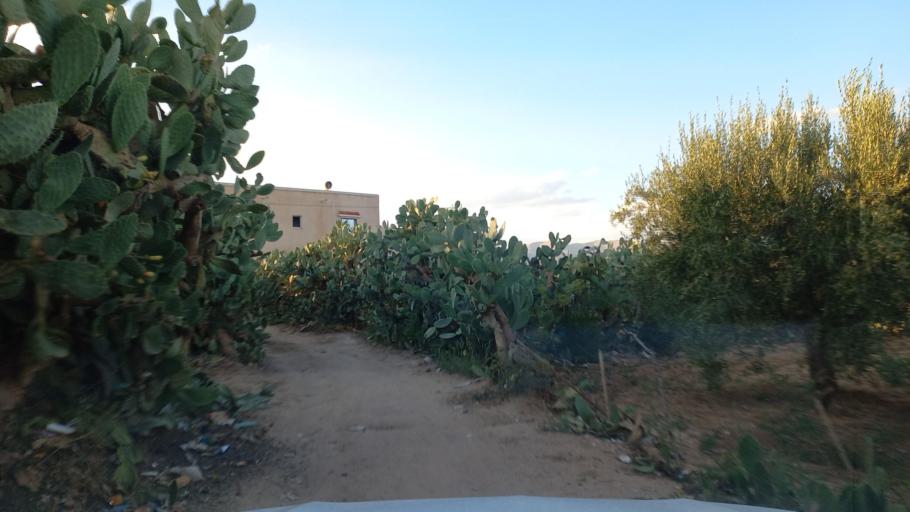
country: TN
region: Al Qasrayn
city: Sbiba
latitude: 35.3792
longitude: 9.0536
